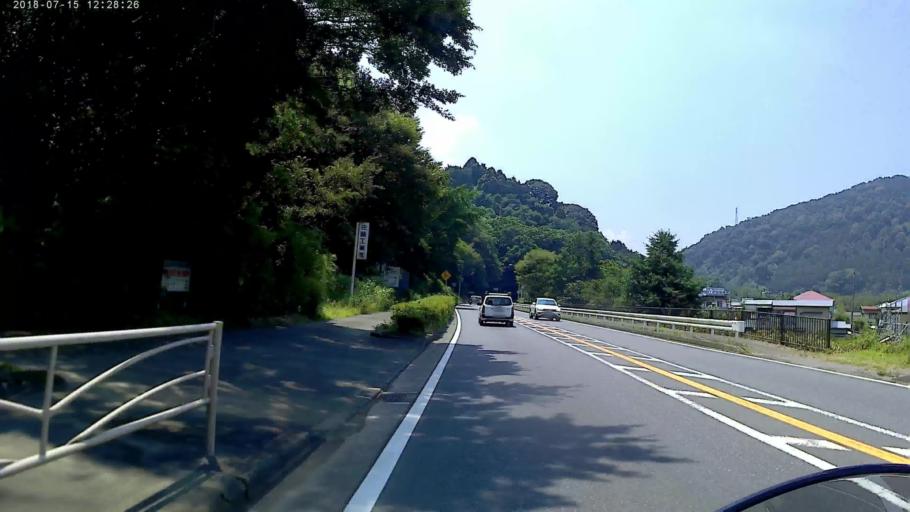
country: JP
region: Kanagawa
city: Odawara
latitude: 35.3592
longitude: 139.0764
